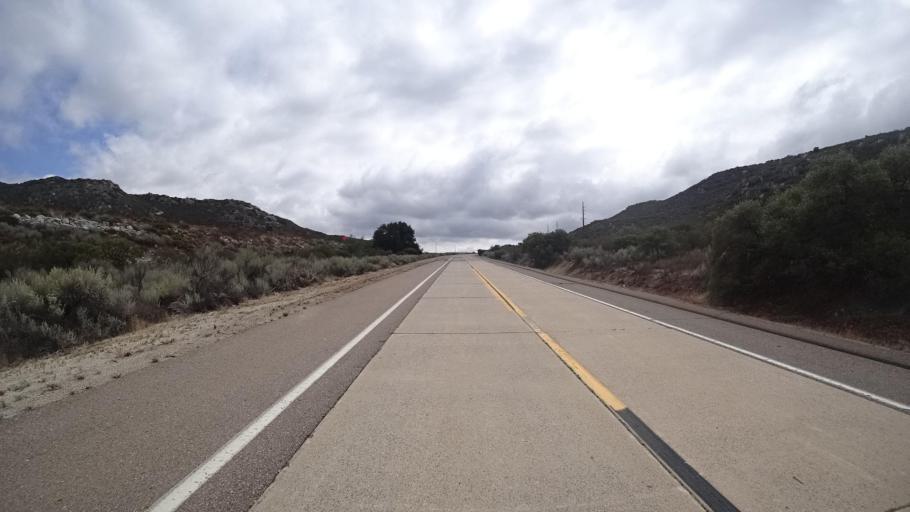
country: US
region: California
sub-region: San Diego County
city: Pine Valley
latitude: 32.7263
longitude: -116.4795
